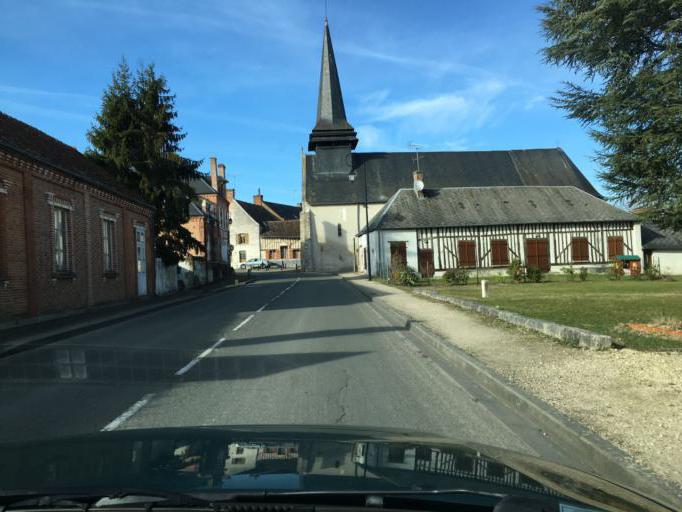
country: FR
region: Centre
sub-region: Departement du Loiret
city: Ligny-le-Ribault
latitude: 47.6835
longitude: 1.7828
